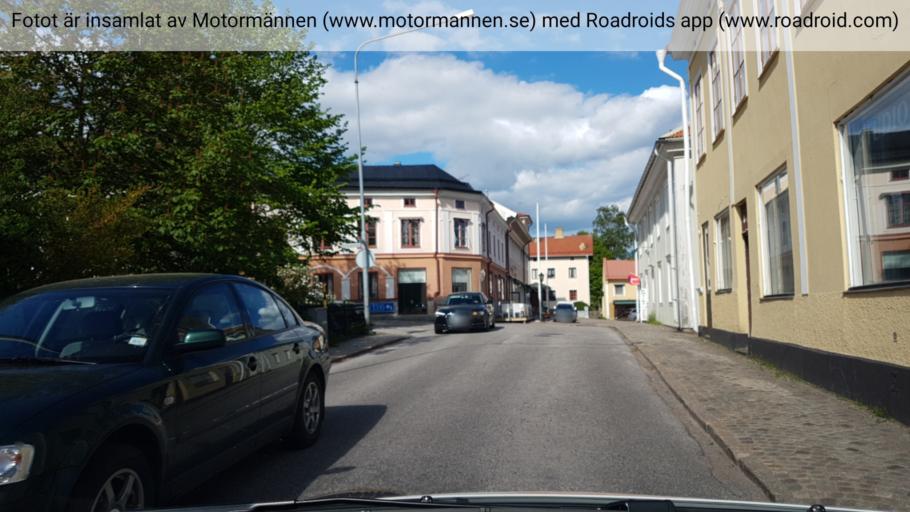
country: SE
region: Kalmar
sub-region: Vasterviks Kommun
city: Gamleby
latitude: 57.8995
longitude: 16.4071
